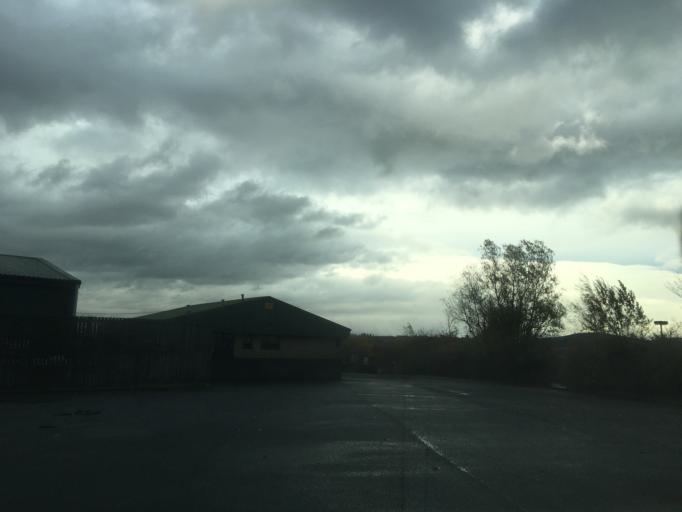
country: GB
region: Scotland
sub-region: Stirling
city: Bridge of Allan
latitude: 56.1399
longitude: -3.9793
